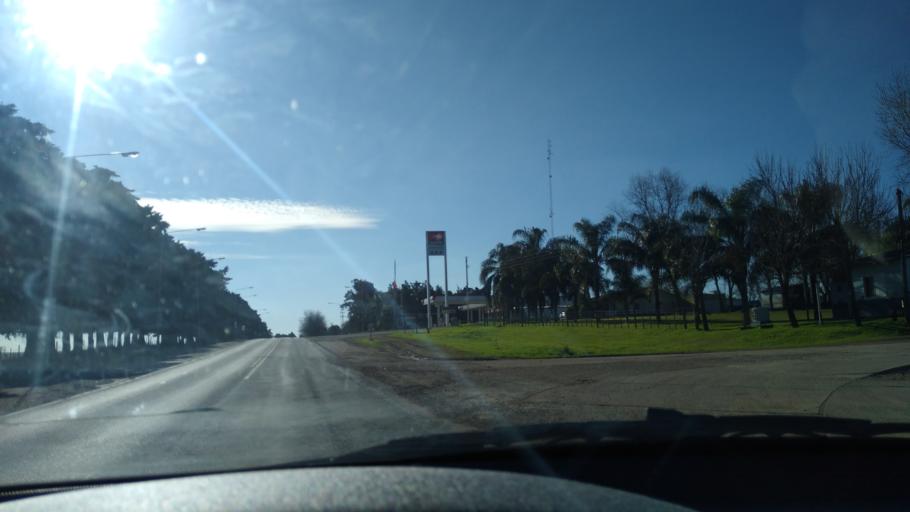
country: AR
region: Entre Rios
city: Aranguren
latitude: -32.4231
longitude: -60.3134
